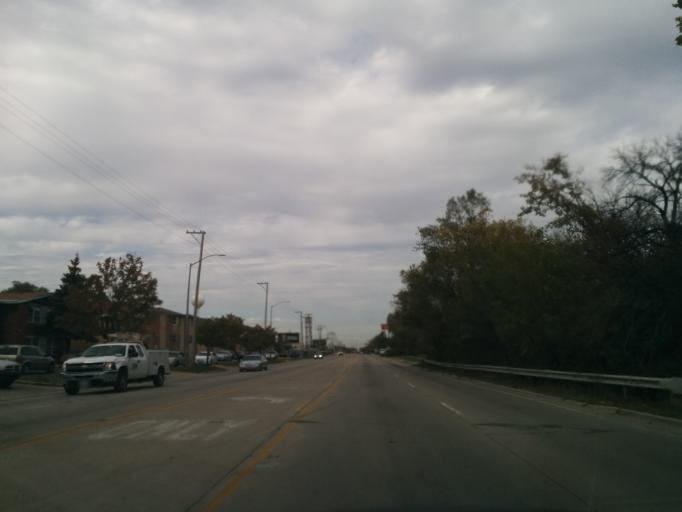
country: US
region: Illinois
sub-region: Cook County
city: River Forest
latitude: 41.9028
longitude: -87.8348
